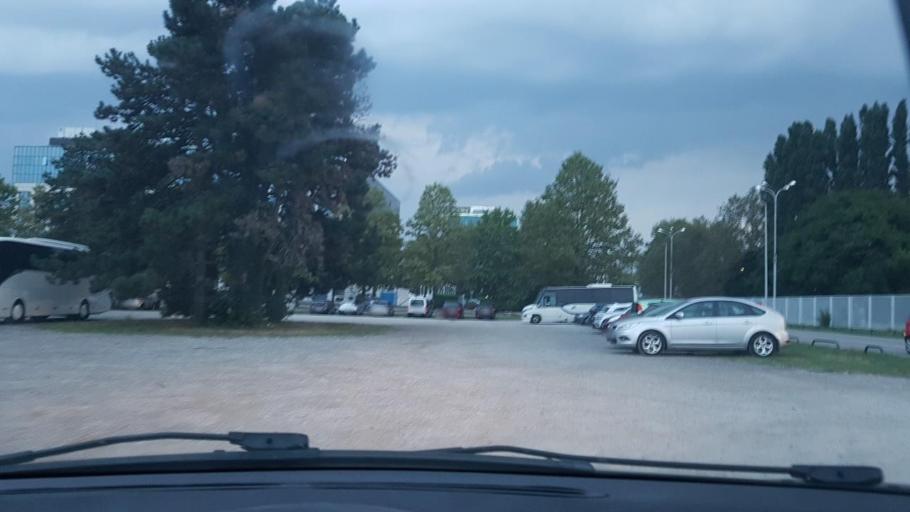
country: HR
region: Grad Zagreb
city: Novi Zagreb
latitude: 45.7802
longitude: 15.9780
